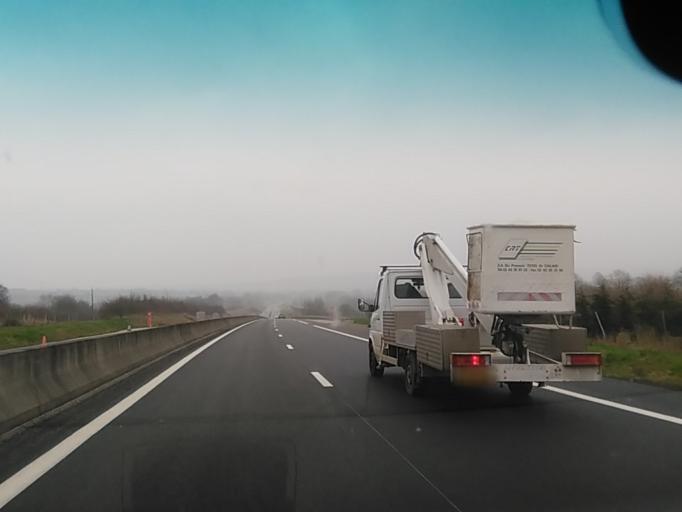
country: FR
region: Lower Normandy
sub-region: Departement de l'Orne
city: Gace
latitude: 48.7493
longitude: 0.2733
